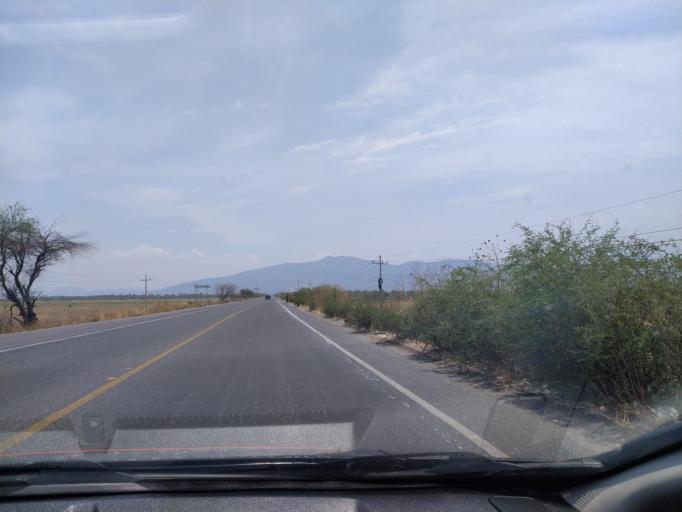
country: MX
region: Jalisco
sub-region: Zacoalco de Torres
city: Barranca de Otates (Barranca de Otatan)
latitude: 20.2981
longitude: -103.6003
